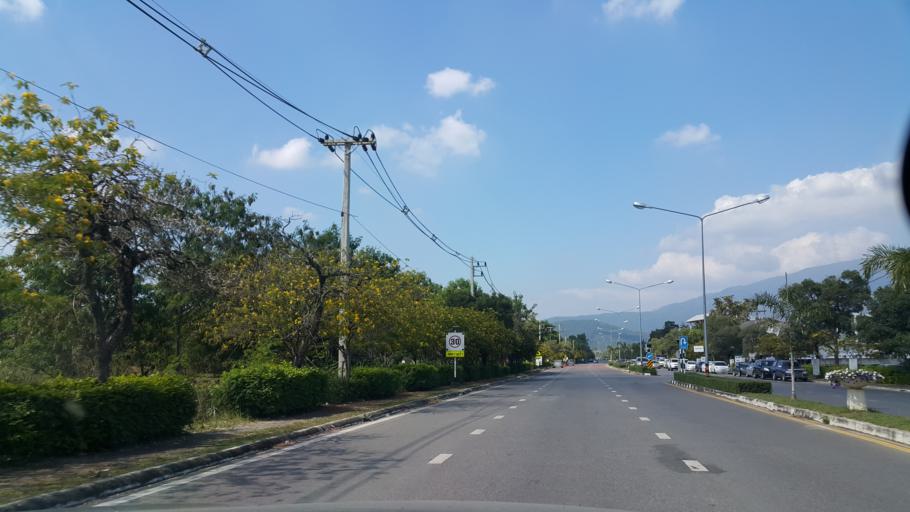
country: TH
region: Chiang Mai
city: Hang Dong
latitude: 18.7298
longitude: 98.9426
